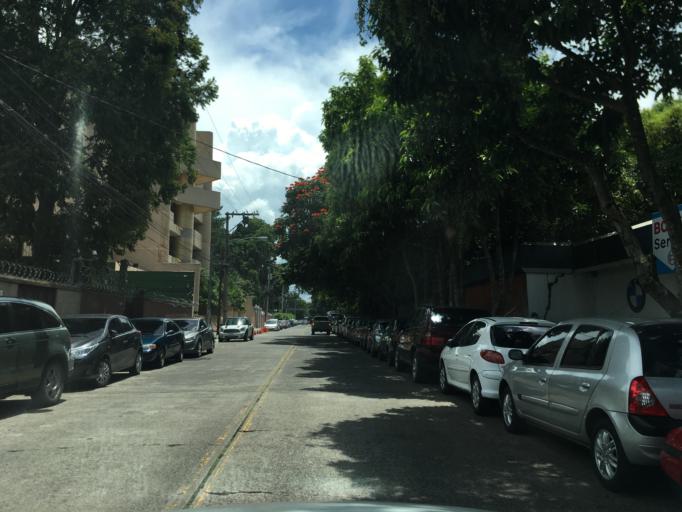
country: GT
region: Guatemala
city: Guatemala City
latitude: 14.6063
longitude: -90.5221
